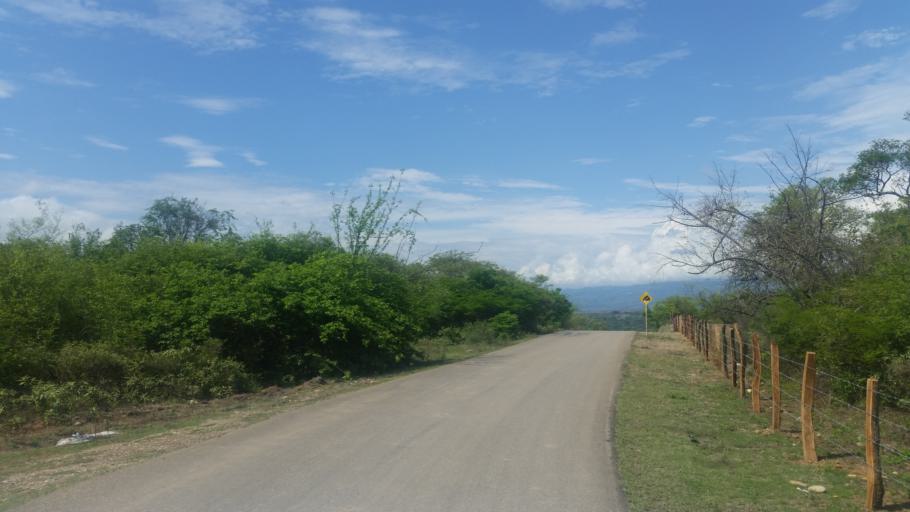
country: CO
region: Huila
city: Villavieja
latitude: 3.2250
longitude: -75.2050
